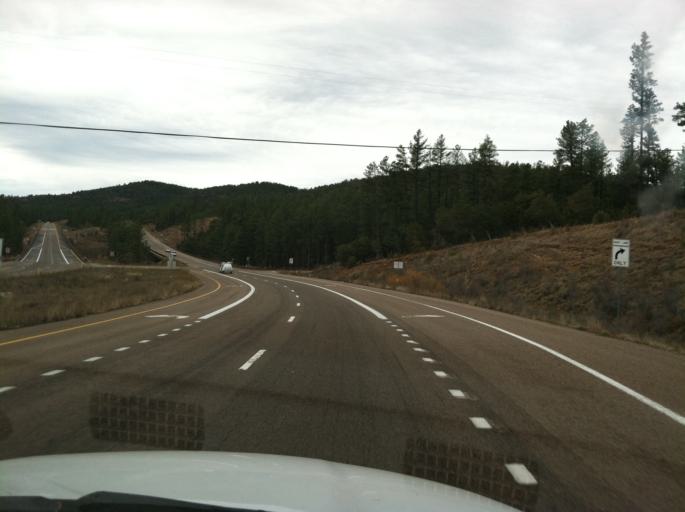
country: US
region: Arizona
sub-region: Gila County
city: Star Valley
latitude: 34.3295
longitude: -111.0904
